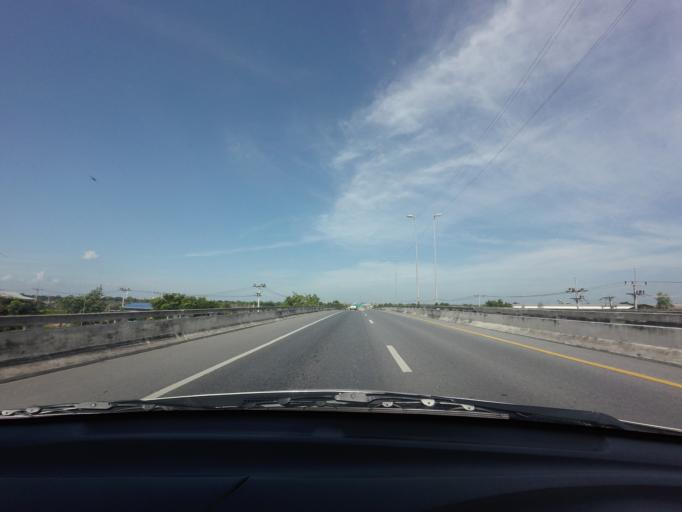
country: TH
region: Suphan Buri
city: Suphan Buri
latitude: 14.4545
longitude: 100.0840
